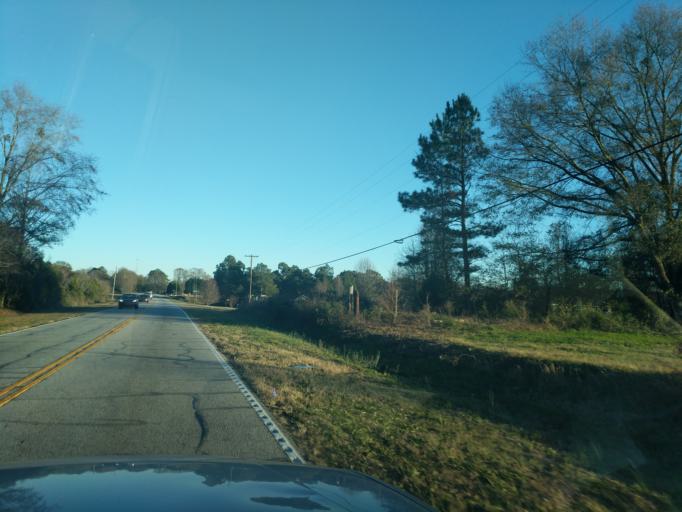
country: US
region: South Carolina
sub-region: Oconee County
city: Utica
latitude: 34.5637
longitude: -82.8844
